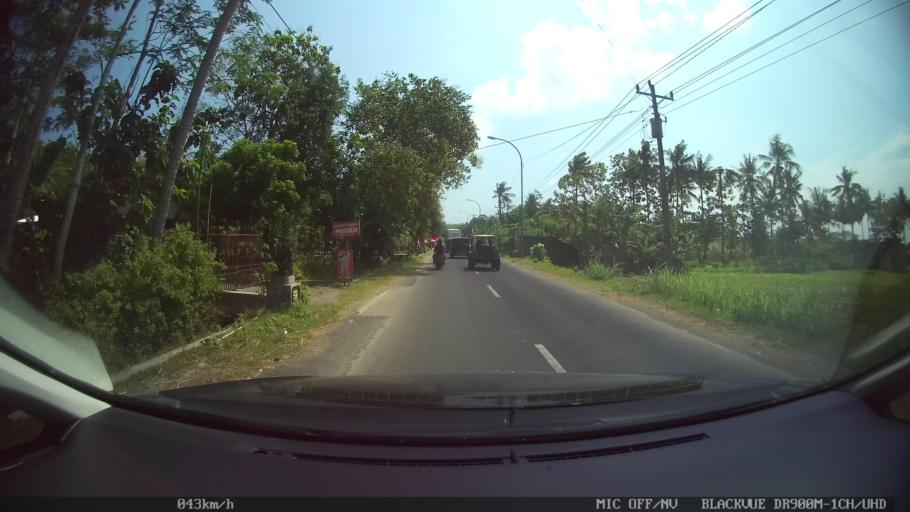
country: ID
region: Daerah Istimewa Yogyakarta
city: Pundong
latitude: -7.9870
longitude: 110.3294
